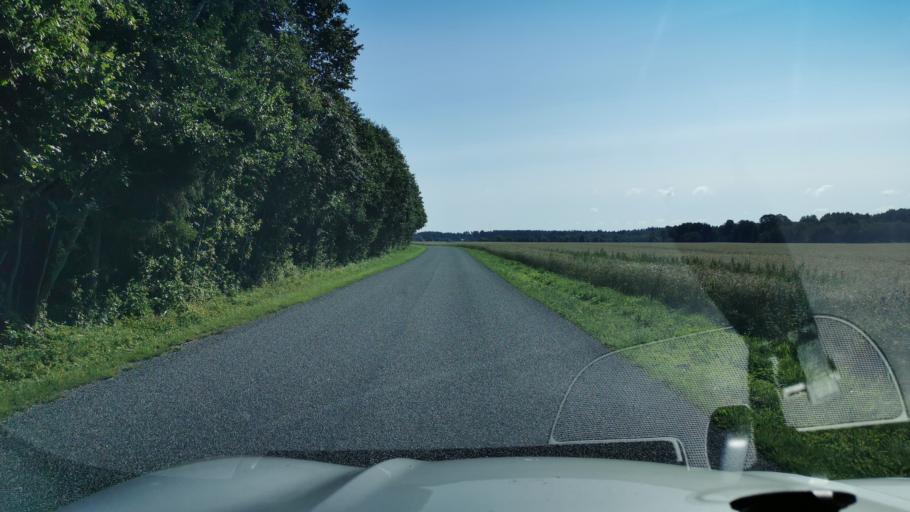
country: EE
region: Harju
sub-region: Paldiski linn
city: Paldiski
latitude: 59.2122
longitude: 24.0262
